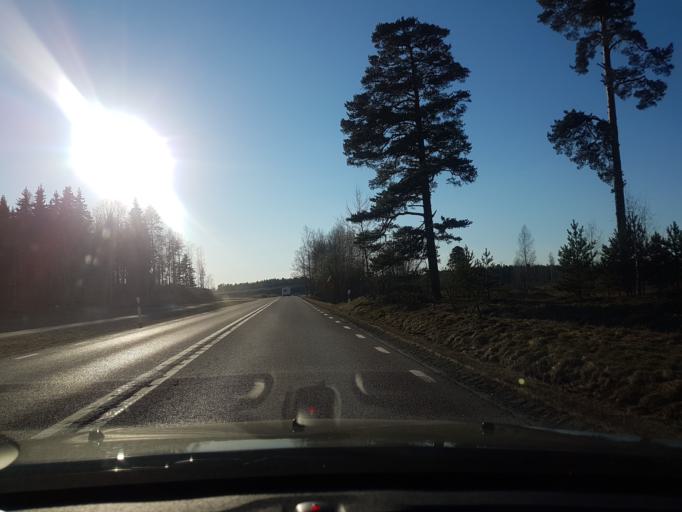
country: SE
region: Uppsala
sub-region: Heby Kommun
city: Morgongava
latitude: 59.9363
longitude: 16.9089
